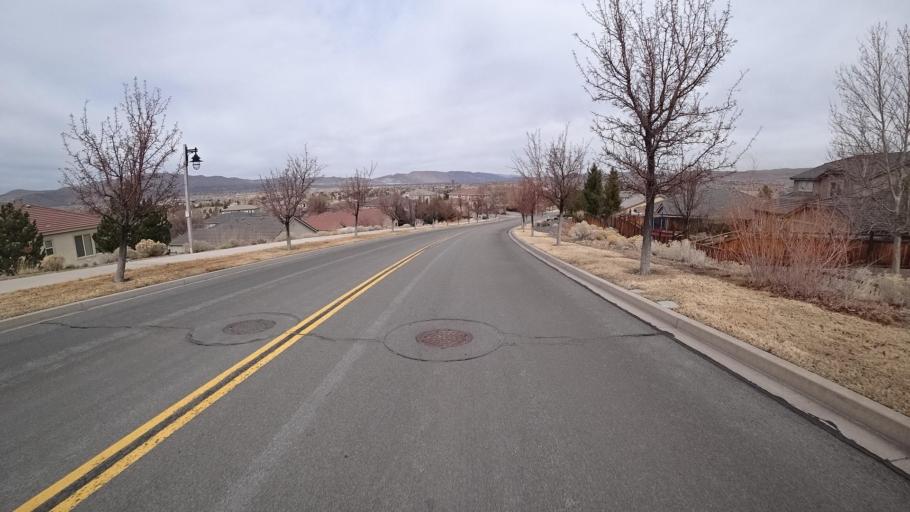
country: US
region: Nevada
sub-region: Washoe County
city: Spanish Springs
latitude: 39.6038
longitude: -119.6866
